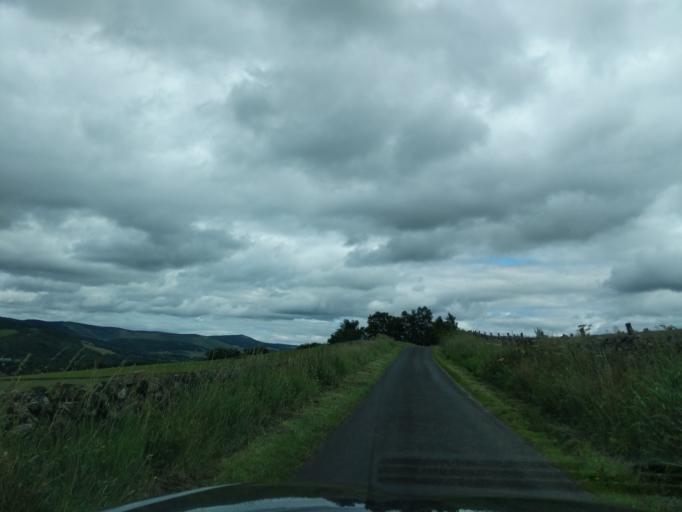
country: GB
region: Scotland
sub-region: The Scottish Borders
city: Peebles
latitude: 55.6457
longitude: -3.2159
